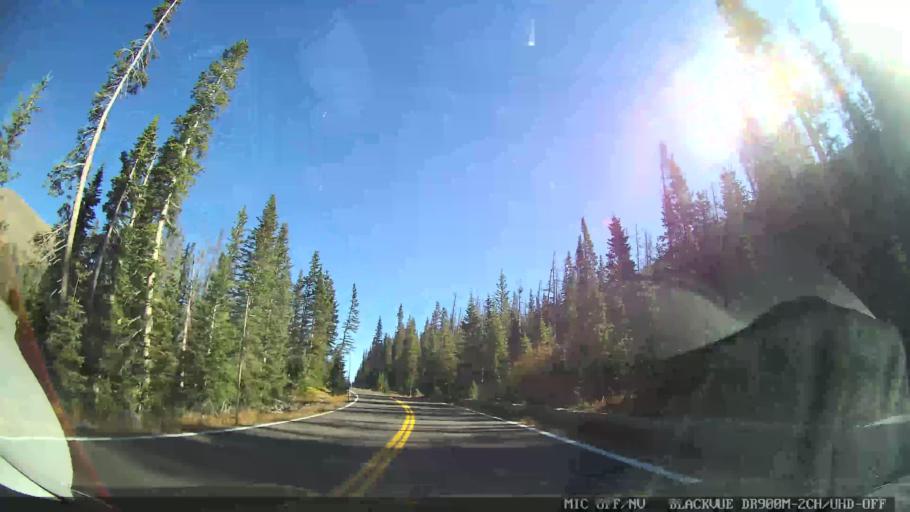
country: US
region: Colorado
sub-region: Larimer County
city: Estes Park
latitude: 40.4283
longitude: -105.7990
